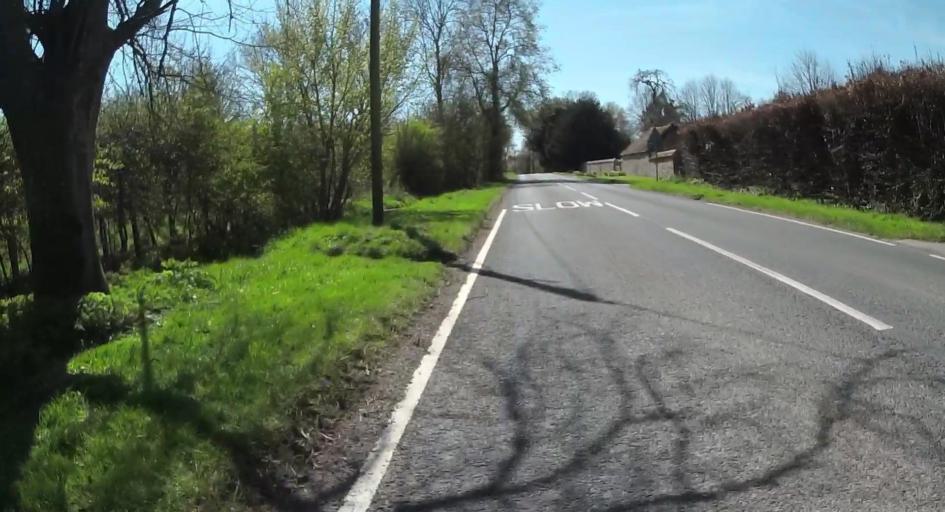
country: GB
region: England
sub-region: Hampshire
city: Chandlers Ford
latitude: 51.0931
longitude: -1.4350
